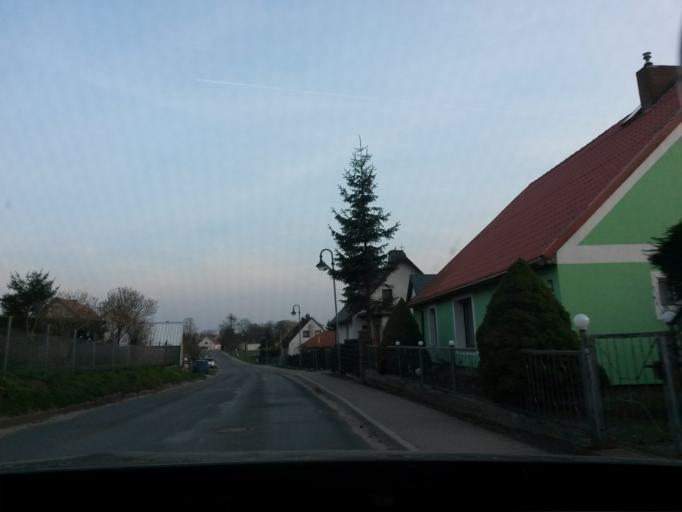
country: DE
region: Brandenburg
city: Protzel
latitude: 52.5935
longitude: 13.9483
